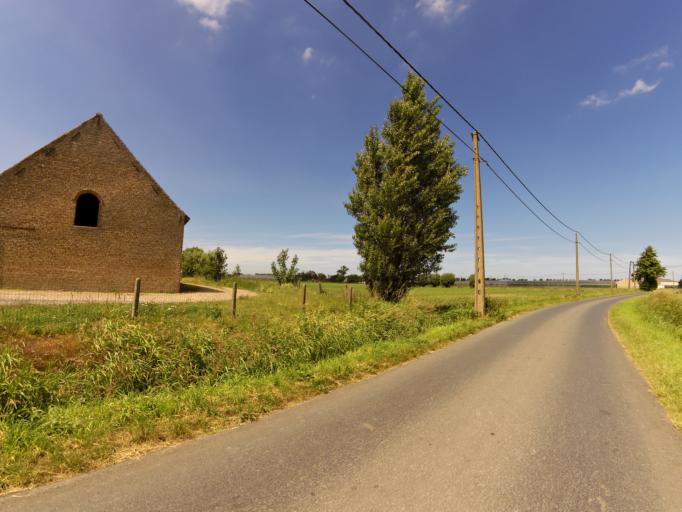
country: BE
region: Flanders
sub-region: Provincie West-Vlaanderen
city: Ichtegem
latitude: 51.1402
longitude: 3.0137
